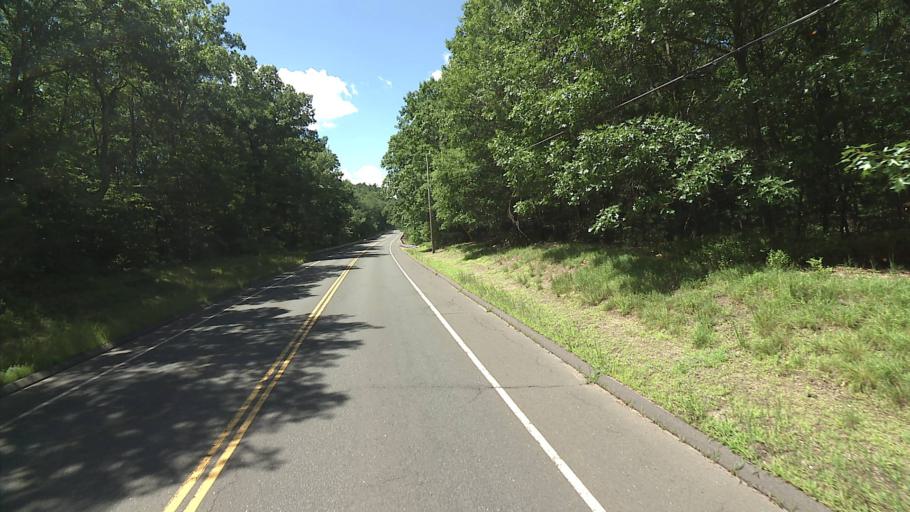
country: US
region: Connecticut
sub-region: Hartford County
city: North Granby
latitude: 41.9545
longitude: -72.8806
